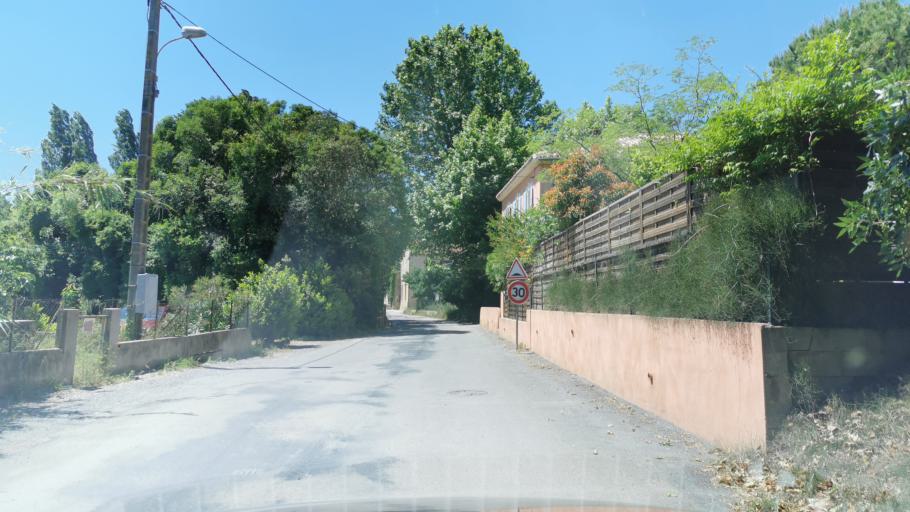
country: FR
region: Languedoc-Roussillon
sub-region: Departement de l'Aude
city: Saint-Marcel-sur-Aude
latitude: 43.2582
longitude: 2.9522
